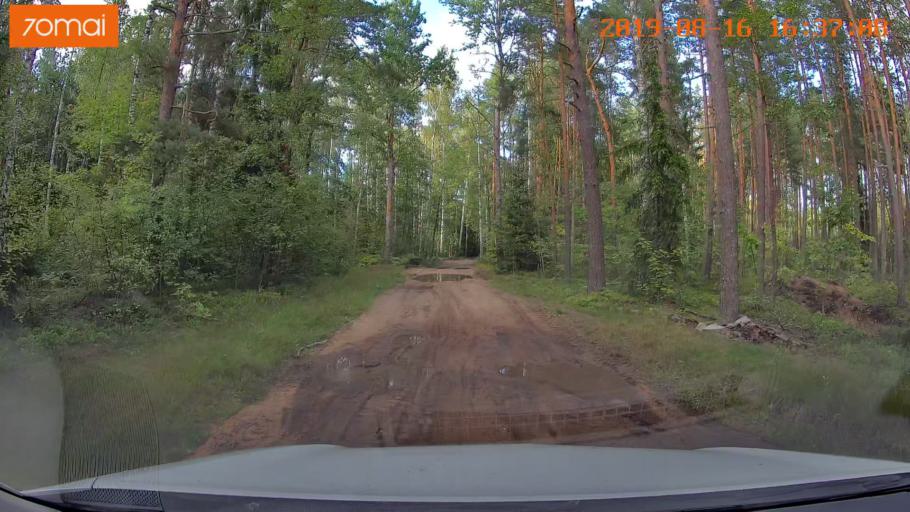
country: BY
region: Mogilev
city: Asipovichy
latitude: 53.2319
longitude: 28.7762
